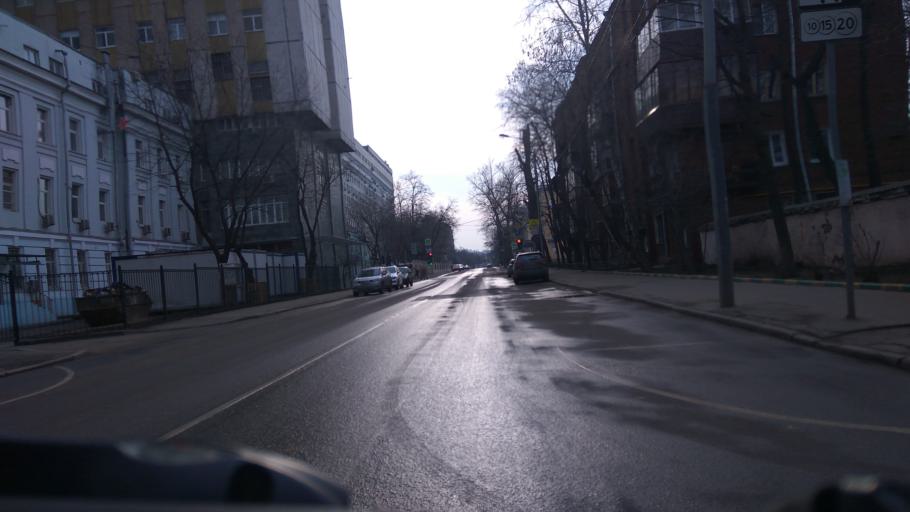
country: RU
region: Moscow
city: Luzhniki
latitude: 55.7308
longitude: 37.5643
